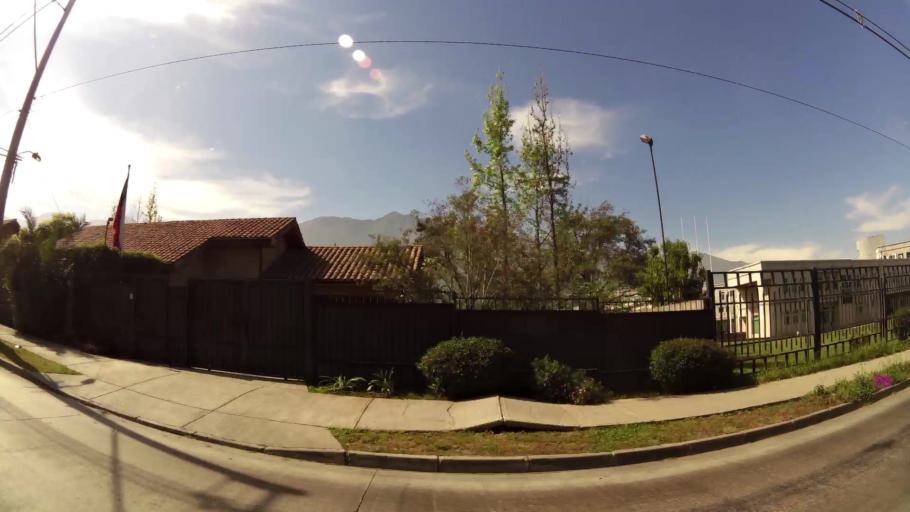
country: CL
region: Santiago Metropolitan
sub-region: Provincia de Santiago
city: Villa Presidente Frei, Nunoa, Santiago, Chile
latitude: -33.4464
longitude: -70.5375
